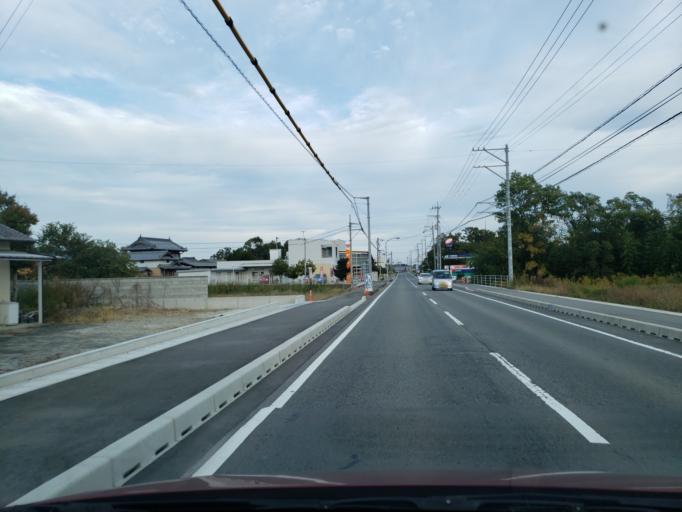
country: JP
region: Tokushima
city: Wakimachi
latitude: 34.0786
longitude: 134.2483
